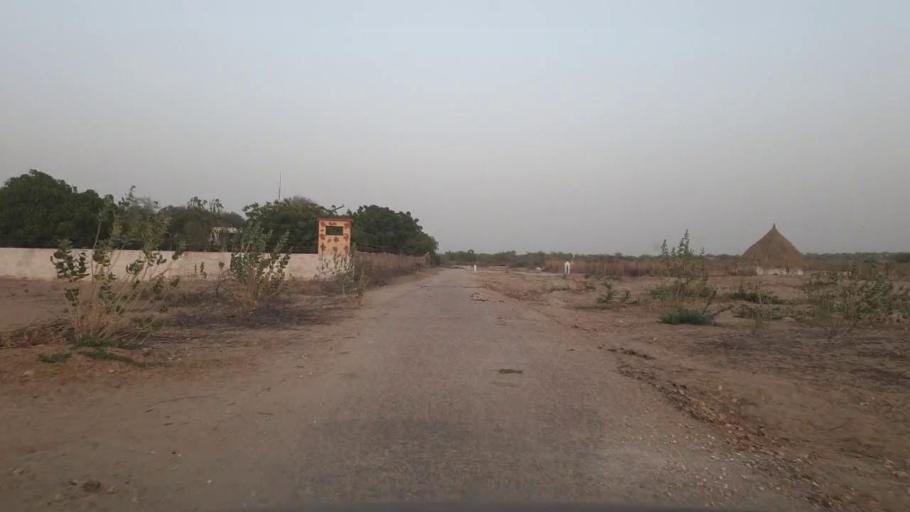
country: PK
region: Sindh
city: Chor
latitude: 25.5229
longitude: 69.8266
